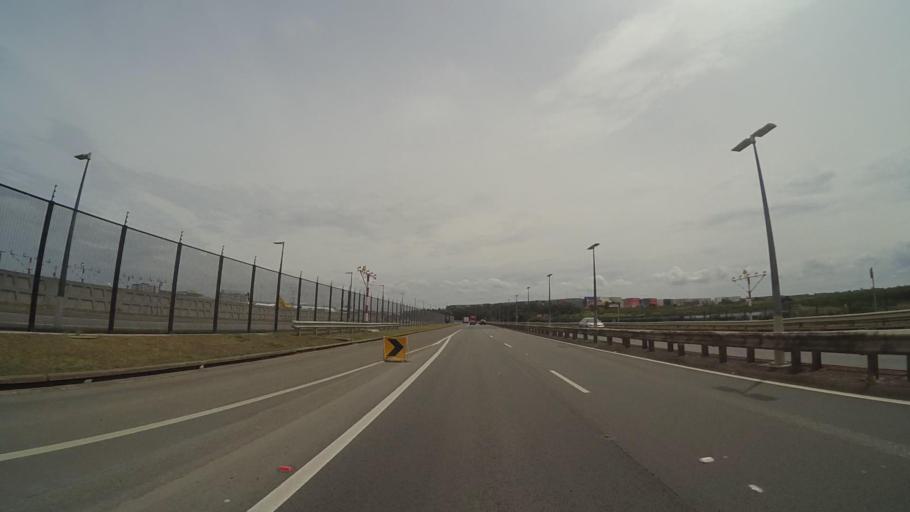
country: AU
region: New South Wales
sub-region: Botany Bay
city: Mascot
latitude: -33.9270
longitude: 151.1713
